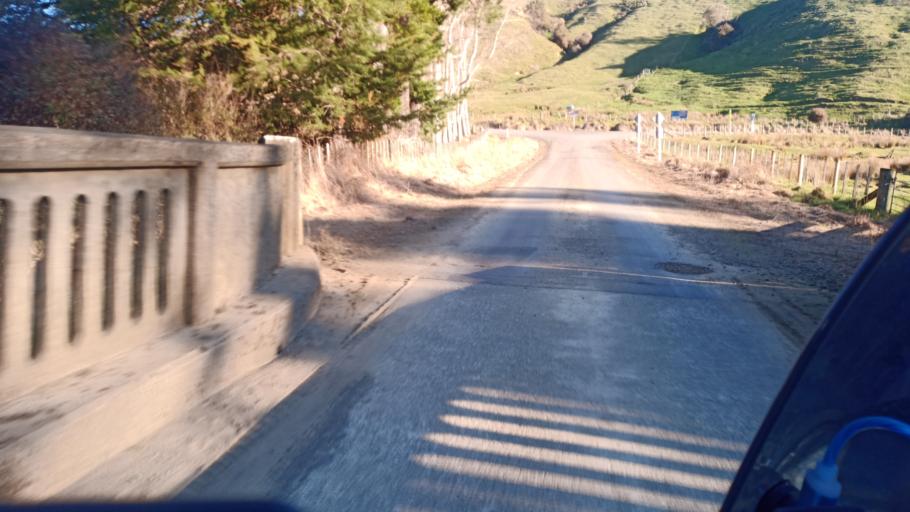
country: NZ
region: Bay of Plenty
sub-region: Opotiki District
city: Opotiki
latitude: -38.4614
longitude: 177.4235
